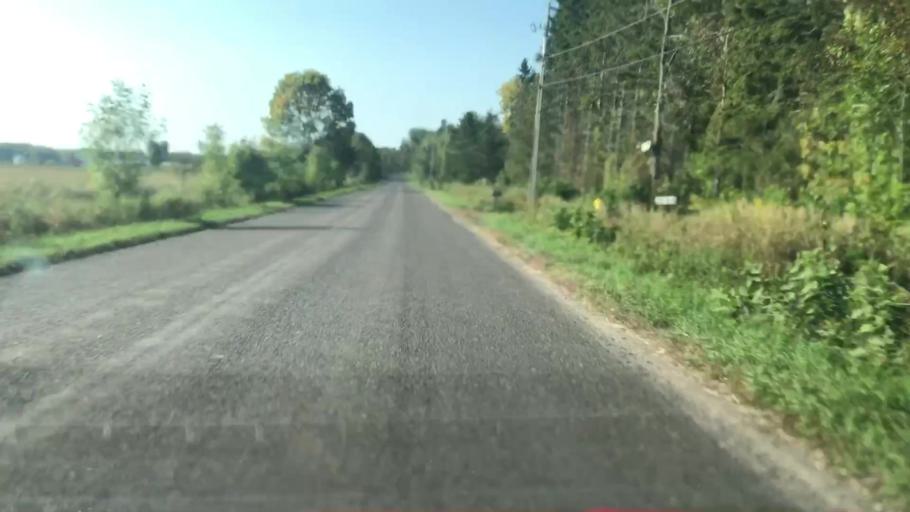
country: US
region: Michigan
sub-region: Chippewa County
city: Sault Ste. Marie
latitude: 46.2901
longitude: -84.0635
